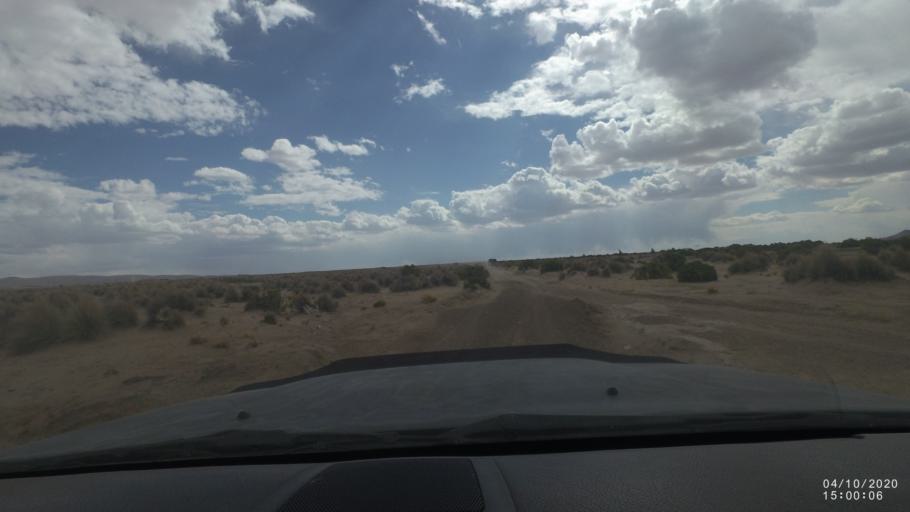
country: BO
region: Oruro
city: Poopo
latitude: -18.6864
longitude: -67.5258
